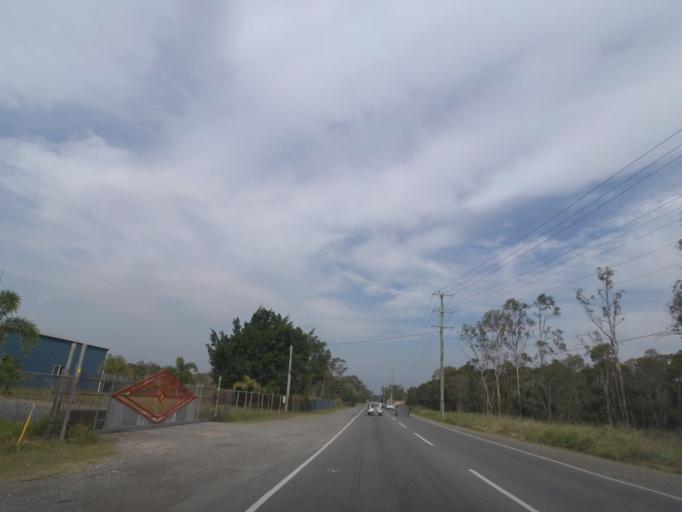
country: AU
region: Queensland
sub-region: Brisbane
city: Inala
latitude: -27.5933
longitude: 152.9980
